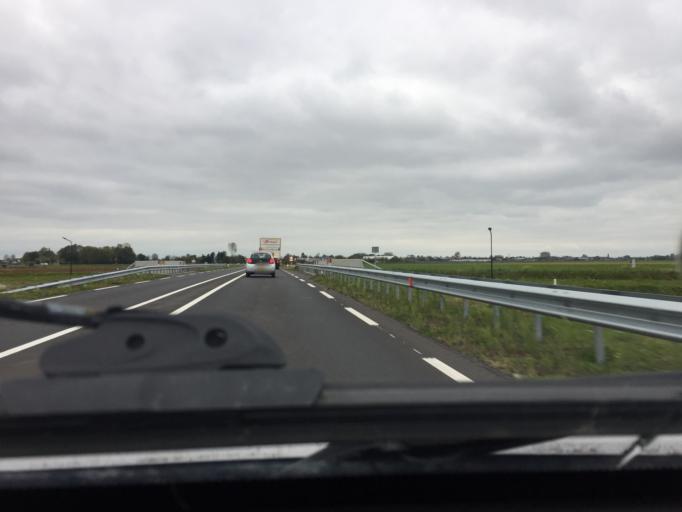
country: NL
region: North Holland
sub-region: Gemeente Heerhugowaard
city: Heerhugowaard
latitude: 52.6817
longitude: 4.8612
